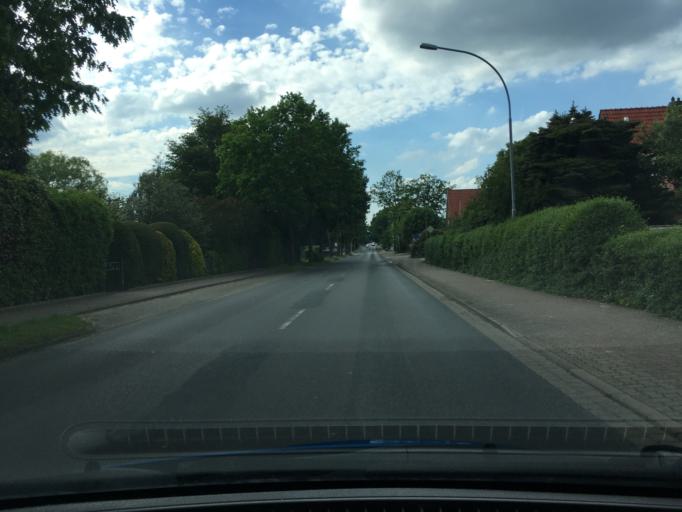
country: DE
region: Lower Saxony
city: Tostedt
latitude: 53.2663
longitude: 9.7300
